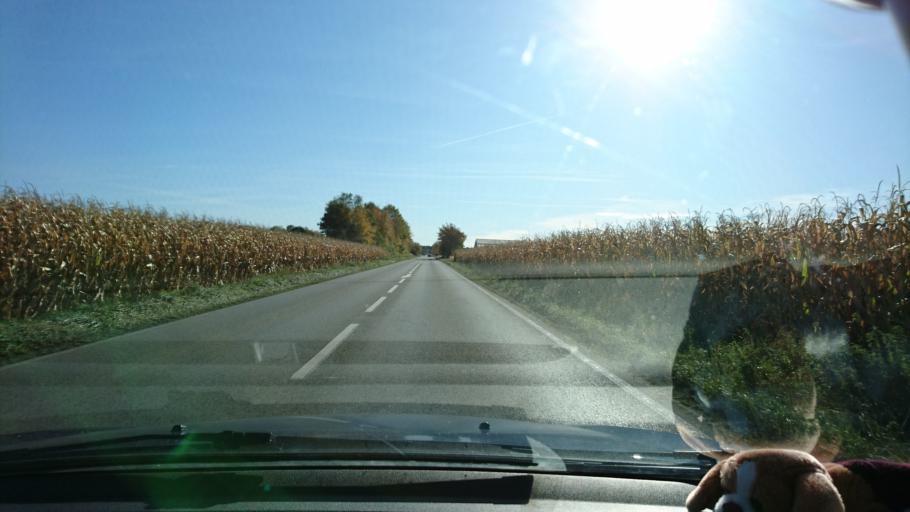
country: DE
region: Bavaria
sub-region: Upper Bavaria
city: Zorneding
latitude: 48.0875
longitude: 11.8178
